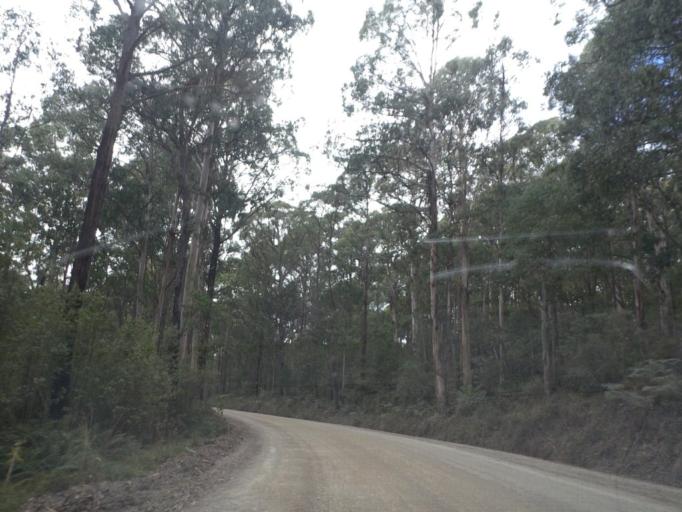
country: AU
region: Victoria
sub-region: Yarra Ranges
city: Millgrove
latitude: -37.5112
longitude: 145.9590
